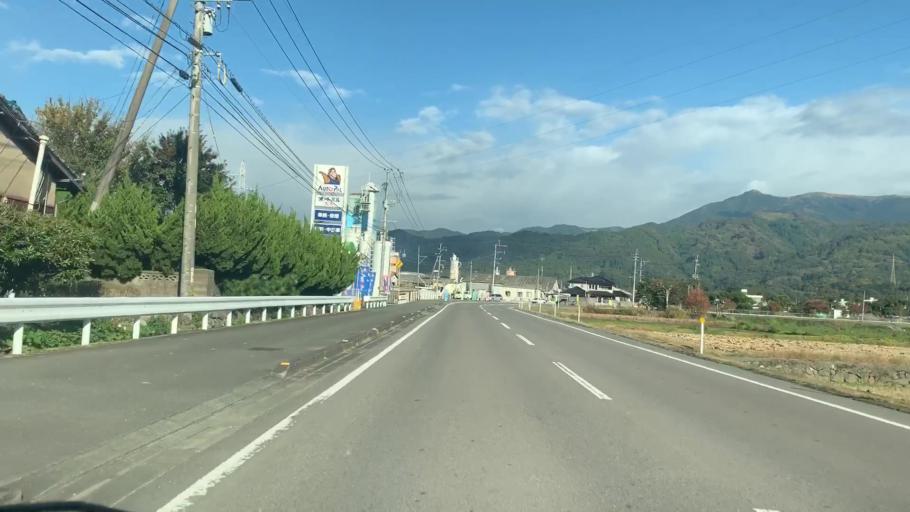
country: JP
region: Saga Prefecture
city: Takeocho-takeo
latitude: 33.2774
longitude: 130.1451
